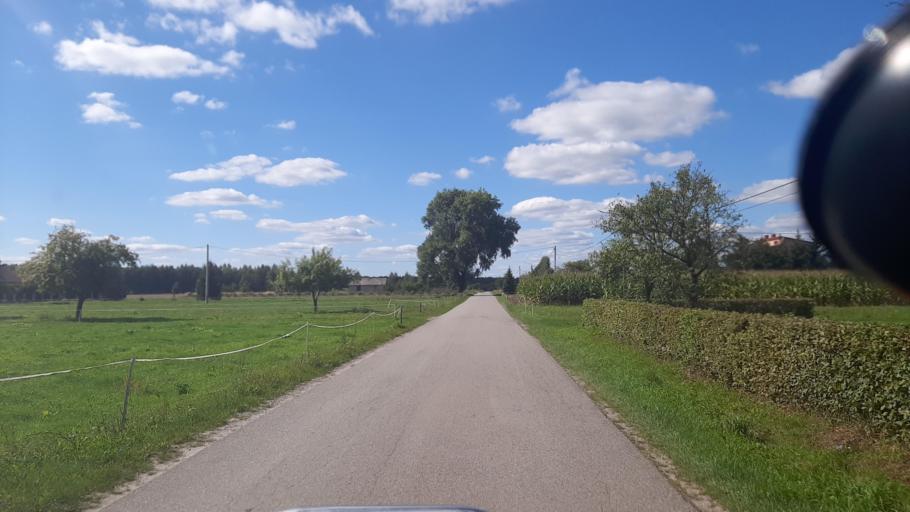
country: PL
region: Lublin Voivodeship
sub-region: Powiat lubelski
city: Garbow
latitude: 51.4068
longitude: 22.3996
